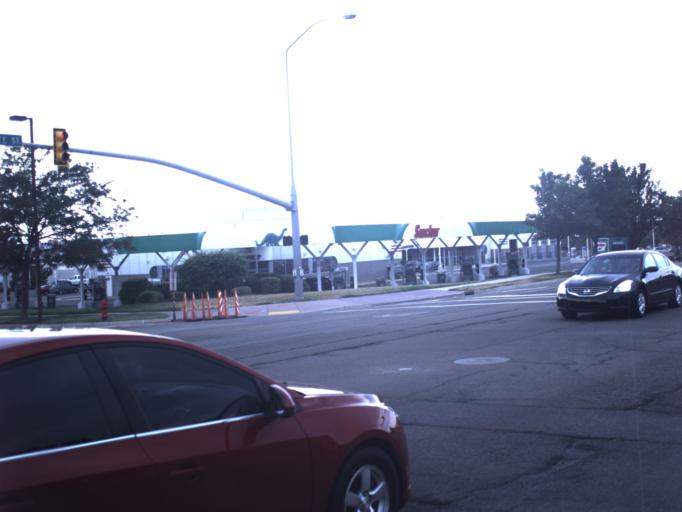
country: US
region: Utah
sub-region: Salt Lake County
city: White City
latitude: 40.5515
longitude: -111.8907
